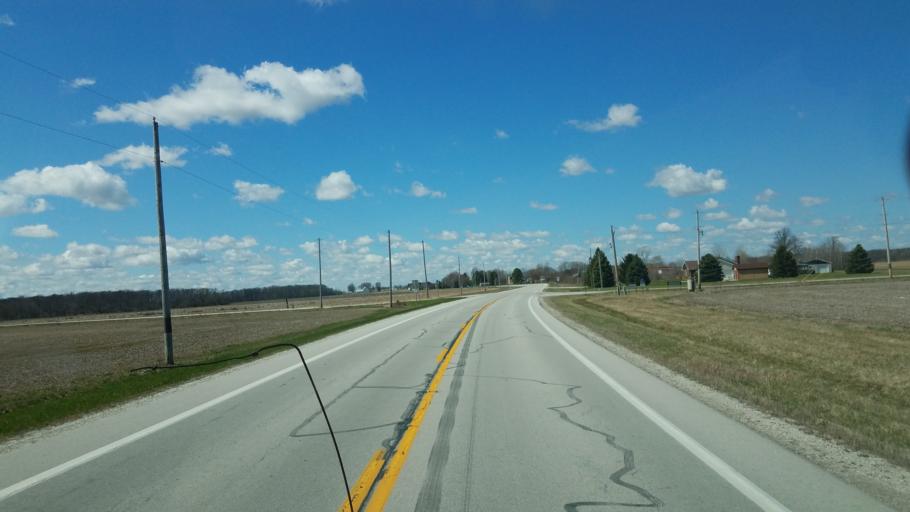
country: US
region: Ohio
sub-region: Seneca County
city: Fostoria
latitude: 41.2065
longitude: -83.3219
